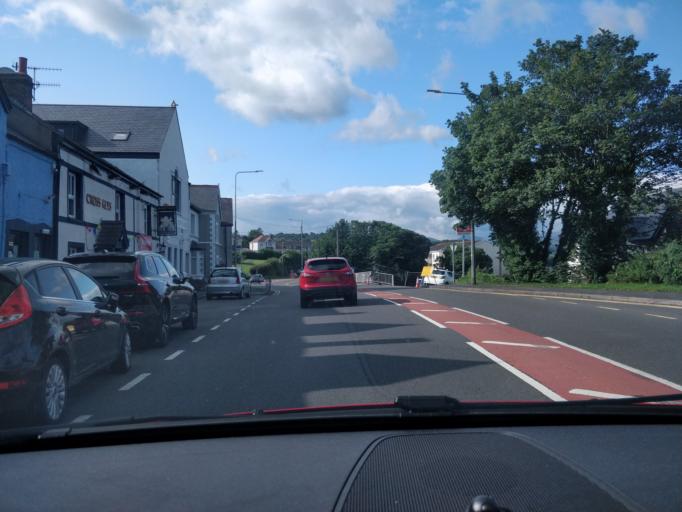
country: GB
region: Wales
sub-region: Conwy
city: Llansantffraid Glan Conwy
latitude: 53.2690
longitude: -3.7963
